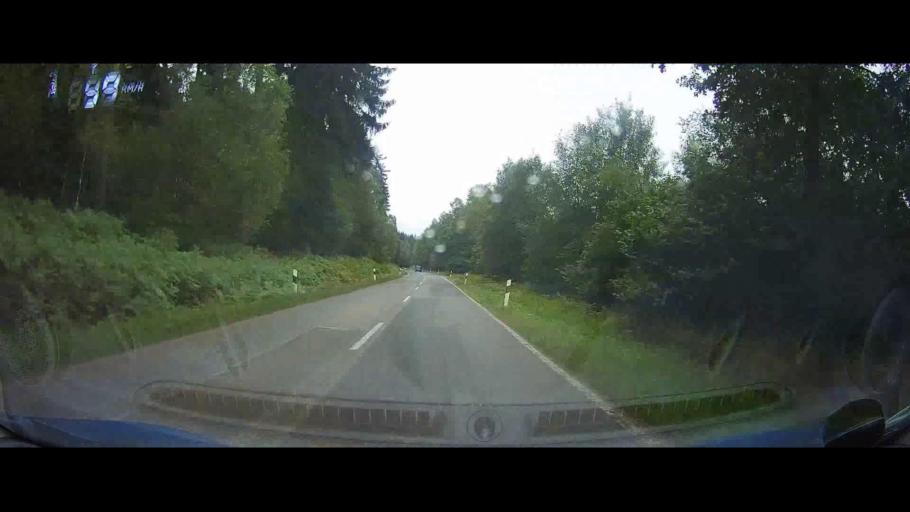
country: DE
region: Lower Saxony
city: Uslar
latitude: 51.7174
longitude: 9.6165
